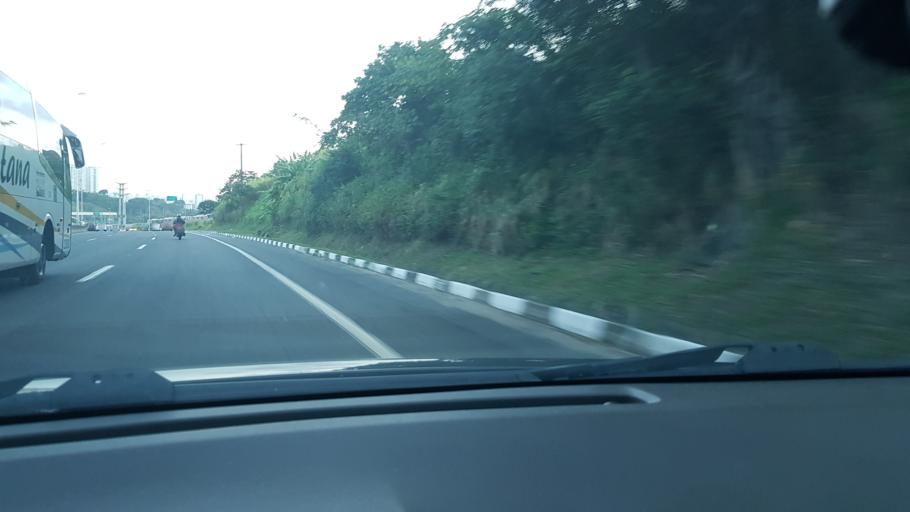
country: BR
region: Bahia
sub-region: Salvador
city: Salvador
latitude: -12.9500
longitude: -38.4705
